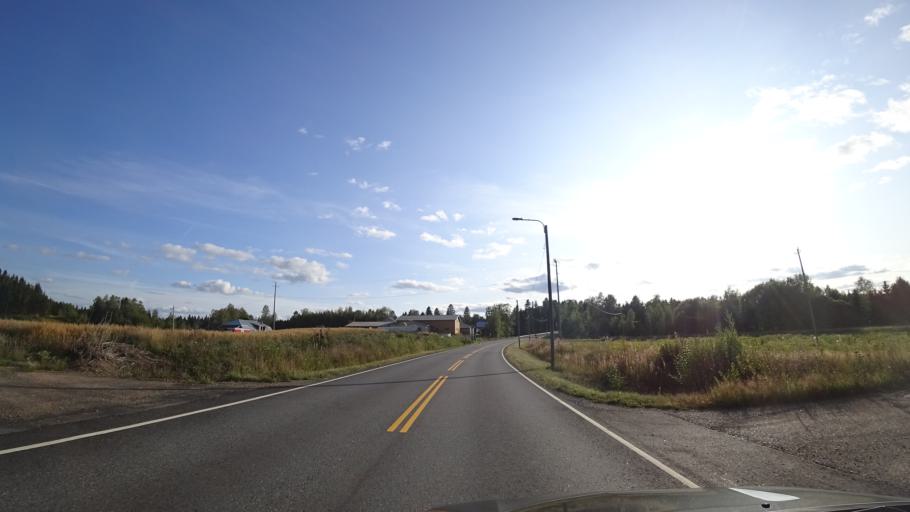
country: FI
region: Paijanne Tavastia
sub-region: Lahti
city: Hollola
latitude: 61.1417
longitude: 25.3294
